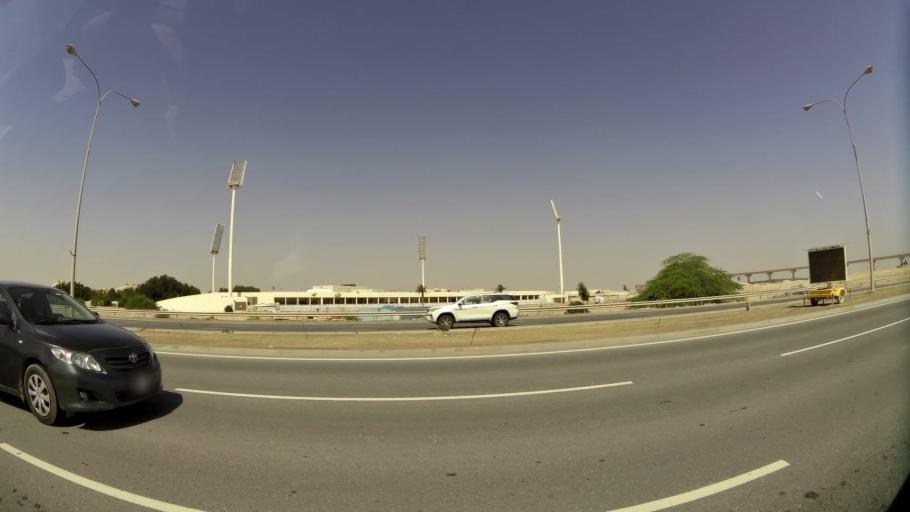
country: QA
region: Baladiyat ad Dawhah
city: Doha
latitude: 25.3747
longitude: 51.4980
